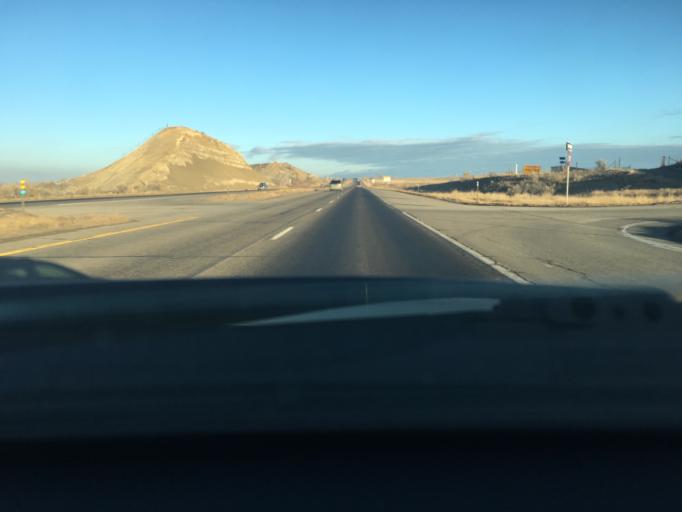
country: US
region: Colorado
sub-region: Montrose County
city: Olathe
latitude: 38.5348
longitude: -107.9384
